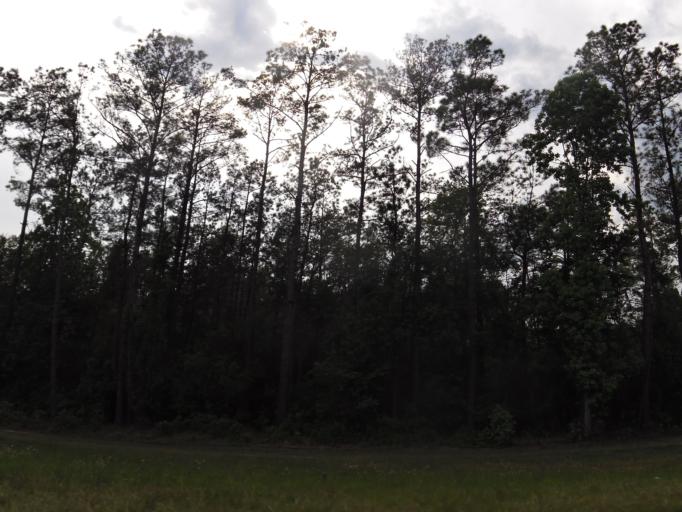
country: US
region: Georgia
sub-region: Charlton County
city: Folkston
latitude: 30.7807
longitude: -81.9791
